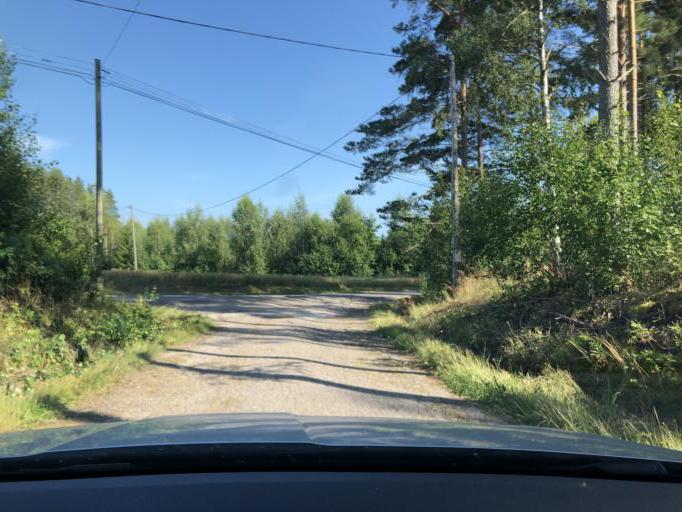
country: SE
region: Dalarna
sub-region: Hedemora Kommun
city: Hedemora
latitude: 60.3260
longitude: 15.9128
